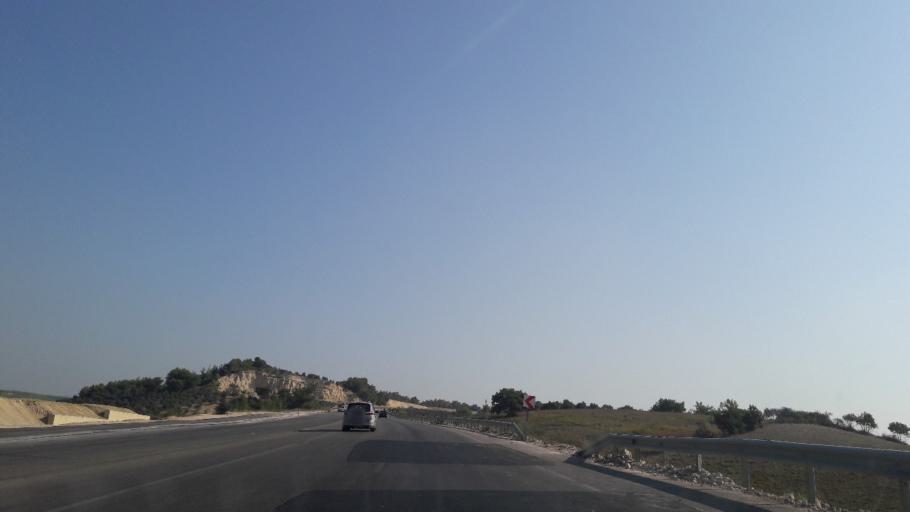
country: TR
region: Adana
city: Yuregir
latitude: 37.0763
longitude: 35.4706
